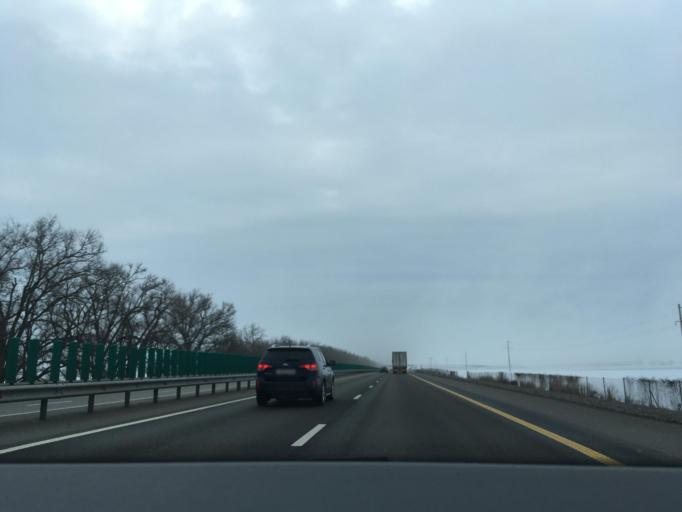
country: RU
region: Krasnodarskiy
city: Kislyakovskaya
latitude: 46.5146
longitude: 39.6922
